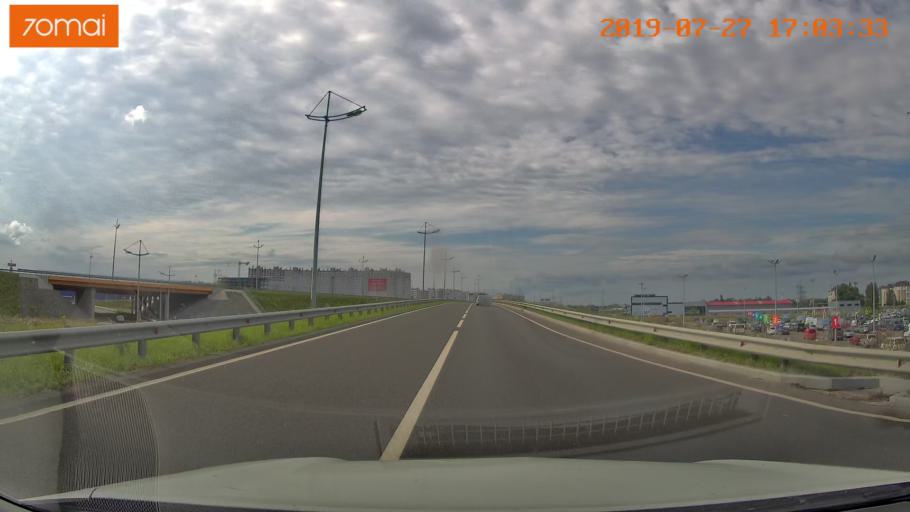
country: RU
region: Kaliningrad
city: Bol'shoe Isakovo
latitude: 54.7056
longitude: 20.6008
